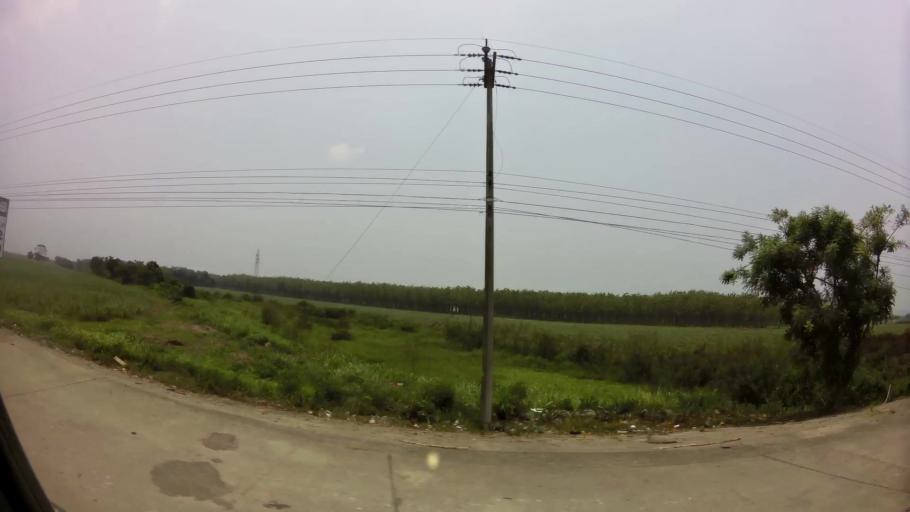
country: HN
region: Cortes
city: La Lima
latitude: 15.4116
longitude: -87.8737
